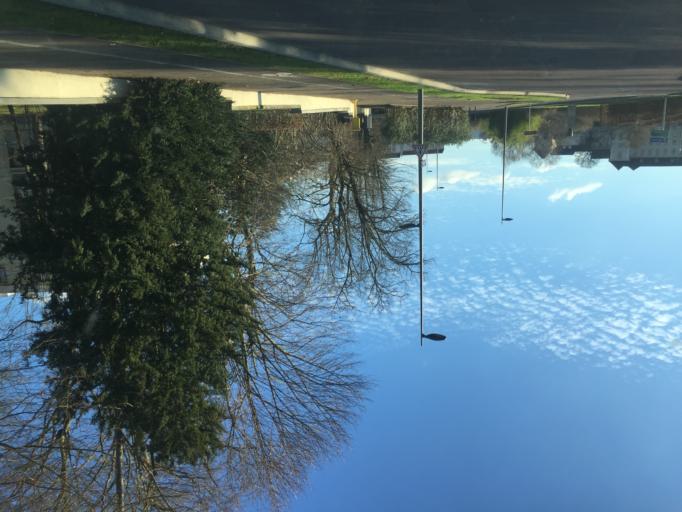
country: FR
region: Bourgogne
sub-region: Departement de l'Yonne
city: Auxerre
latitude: 47.8016
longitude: 3.5774
